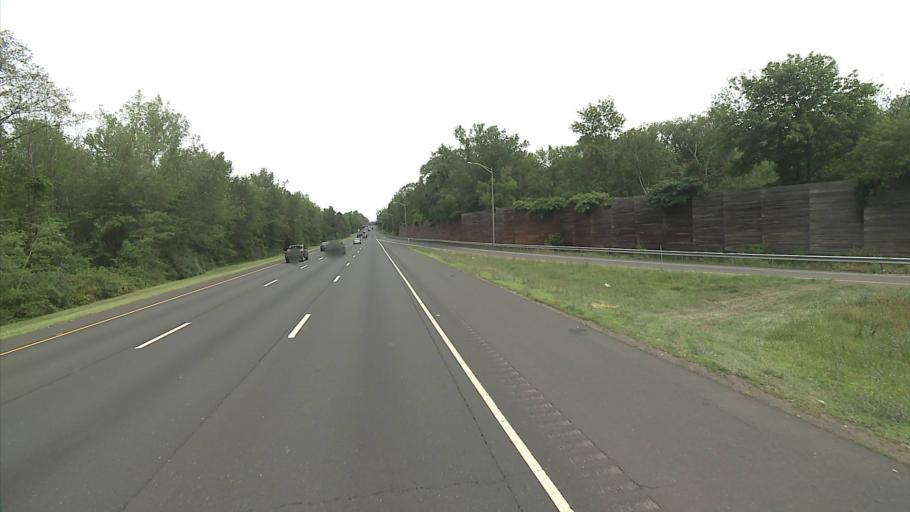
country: US
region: Connecticut
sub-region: Hartford County
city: Plainville
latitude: 41.6776
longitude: -72.8186
